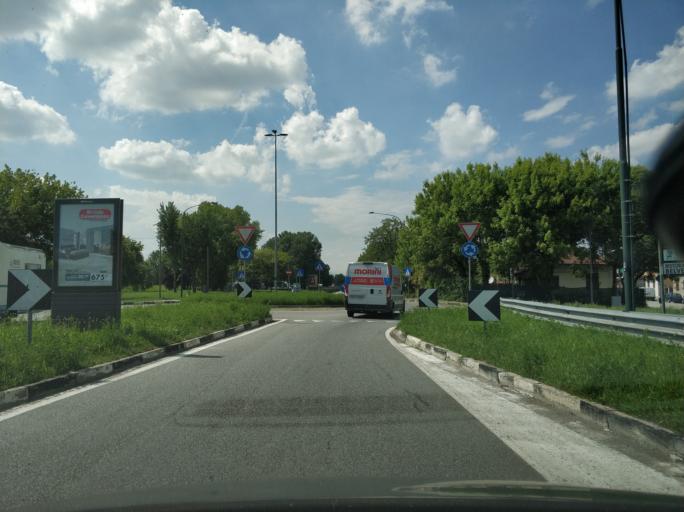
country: IT
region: Piedmont
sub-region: Provincia di Torino
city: San Mauro Torinese
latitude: 45.0963
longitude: 7.7269
